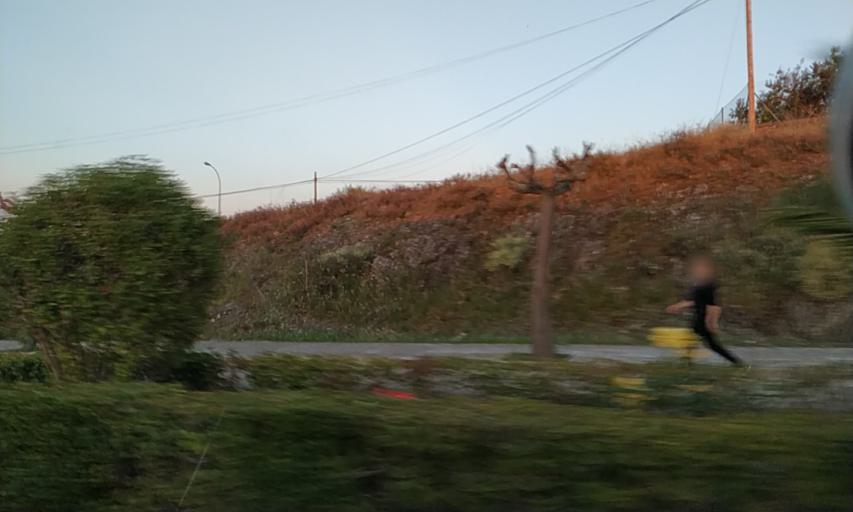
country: ES
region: Extremadura
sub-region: Provincia de Caceres
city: Alcantara
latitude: 39.7112
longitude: -6.8859
